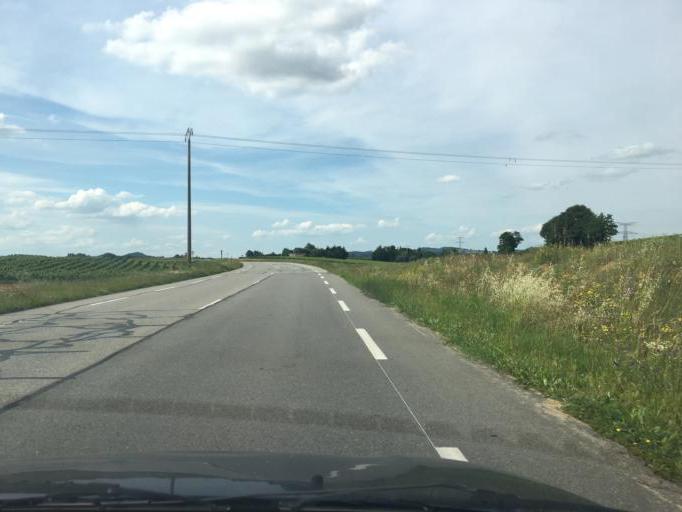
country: FR
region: Rhone-Alpes
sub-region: Departement de la Drome
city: Clerieux
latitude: 45.0845
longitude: 4.9371
